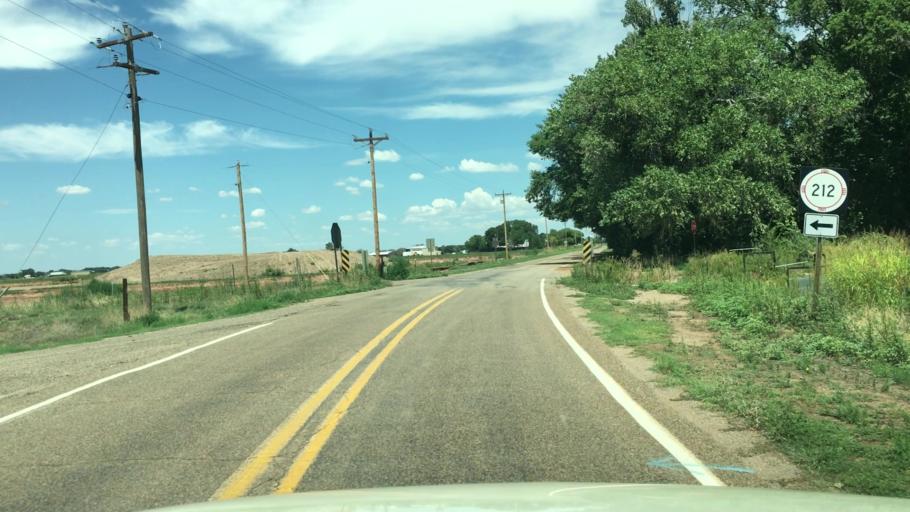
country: US
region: New Mexico
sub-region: De Baca County
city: Fort Sumner
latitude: 34.4046
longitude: -104.1933
